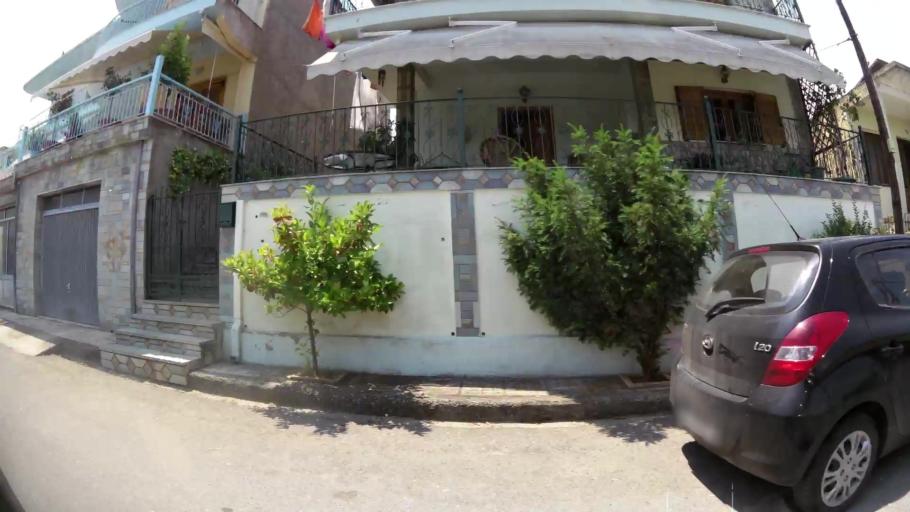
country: GR
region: Central Macedonia
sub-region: Nomos Imathias
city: Veroia
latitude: 40.5145
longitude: 22.1882
